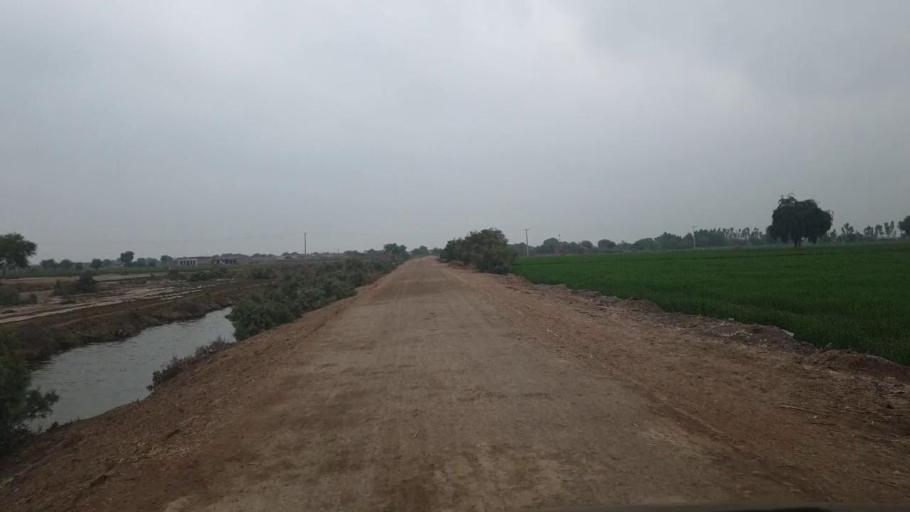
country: PK
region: Sindh
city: Shahdadpur
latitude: 25.9030
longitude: 68.6911
